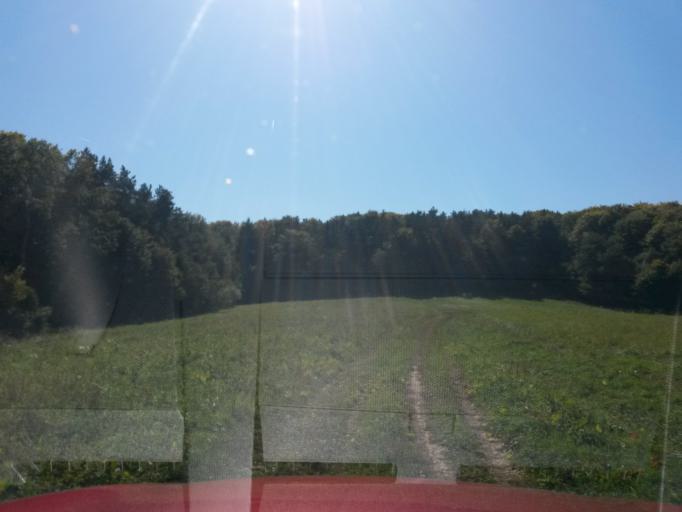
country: SK
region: Presovsky
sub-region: Okres Presov
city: Presov
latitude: 48.9804
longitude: 21.1481
